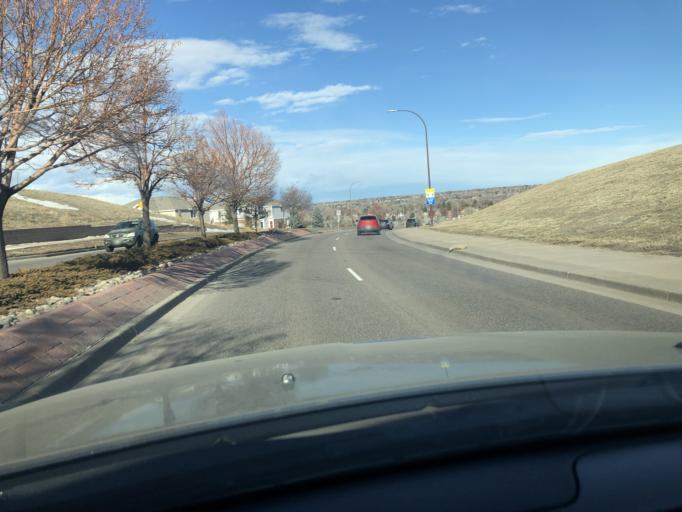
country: US
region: Colorado
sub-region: Jefferson County
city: Arvada
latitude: 39.7967
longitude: -105.1124
